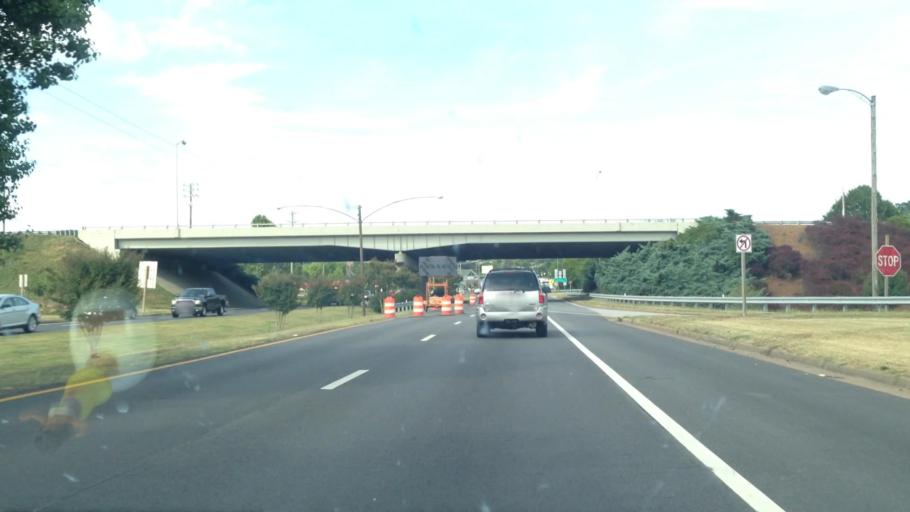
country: US
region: Virginia
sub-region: City of Danville
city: Danville
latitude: 36.5912
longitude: -79.4174
